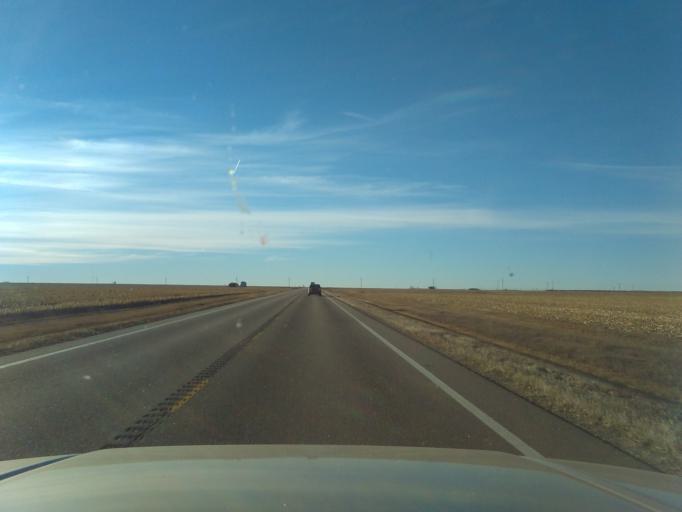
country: US
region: Kansas
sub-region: Thomas County
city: Colby
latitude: 39.4649
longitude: -100.7499
